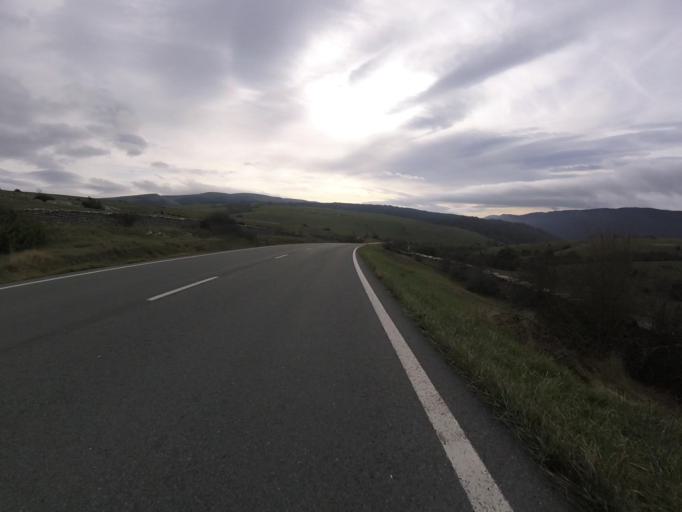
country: ES
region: Navarre
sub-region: Provincia de Navarra
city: Arbizu
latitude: 42.8478
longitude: -2.0160
